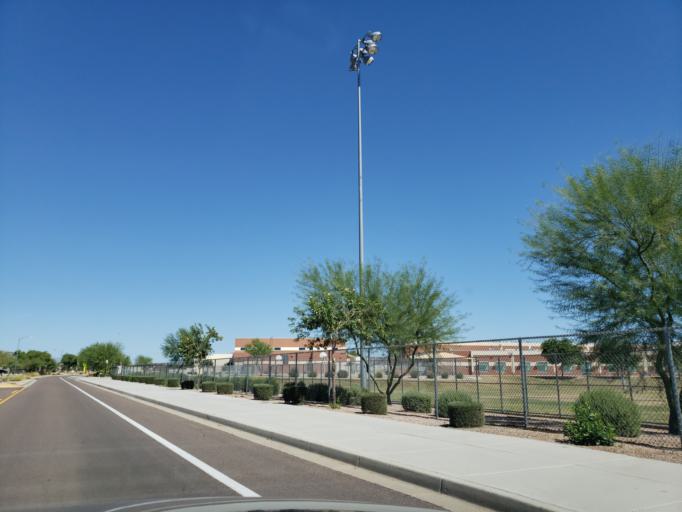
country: US
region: Arizona
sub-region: Maricopa County
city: Sun City West
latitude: 33.6776
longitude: -112.2704
